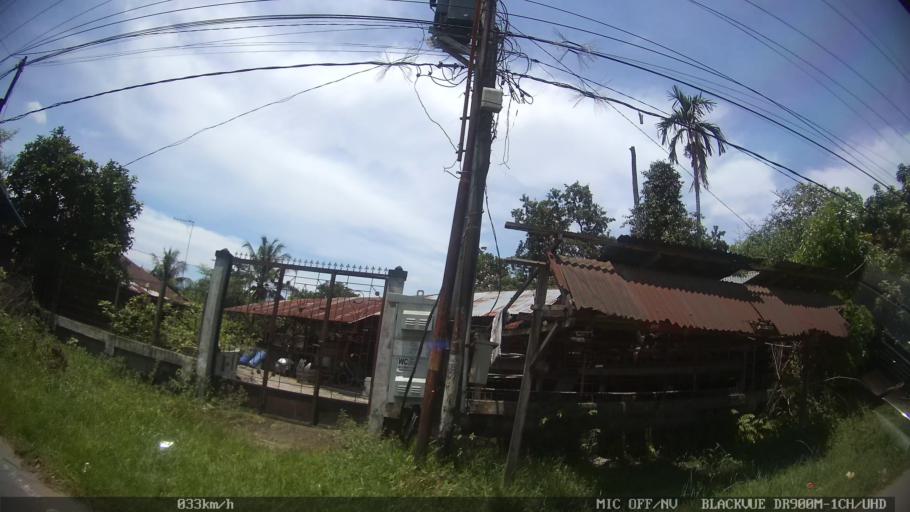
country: ID
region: North Sumatra
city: Binjai
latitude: 3.5945
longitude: 98.5021
